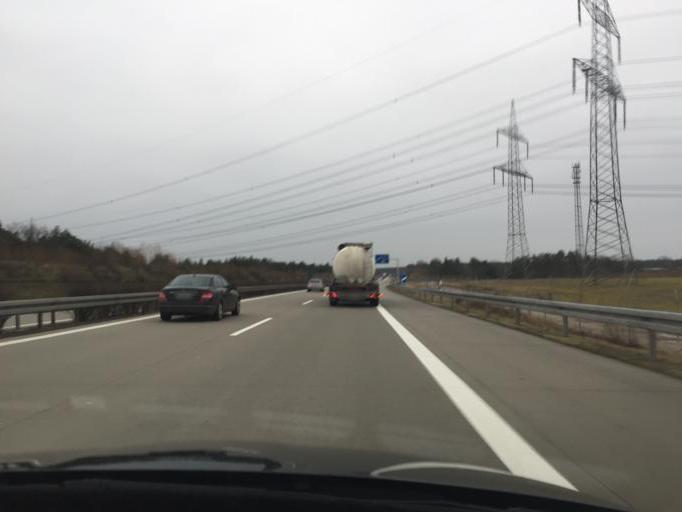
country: DE
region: Brandenburg
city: Luebben
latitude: 51.9037
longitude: 13.8069
